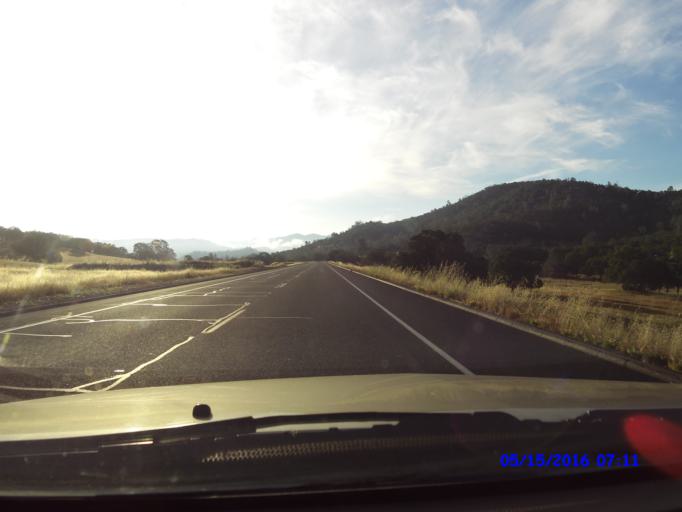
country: US
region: California
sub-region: Tuolumne County
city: Jamestown
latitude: 37.8507
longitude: -120.4062
